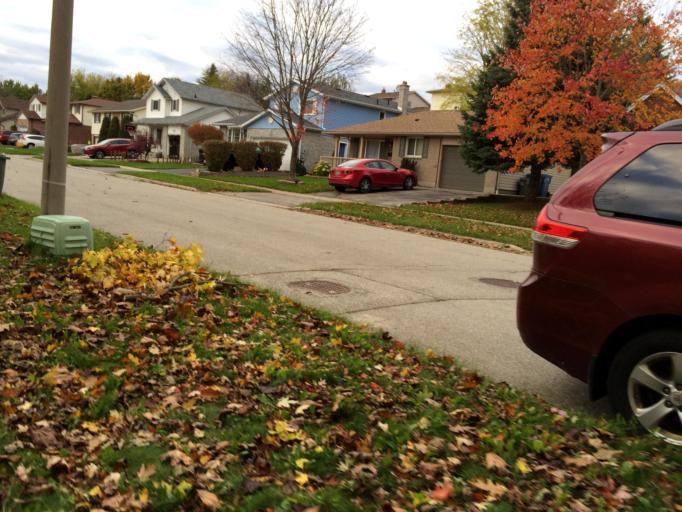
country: CA
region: Ontario
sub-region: Wellington County
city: Guelph
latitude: 43.5315
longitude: -80.2975
